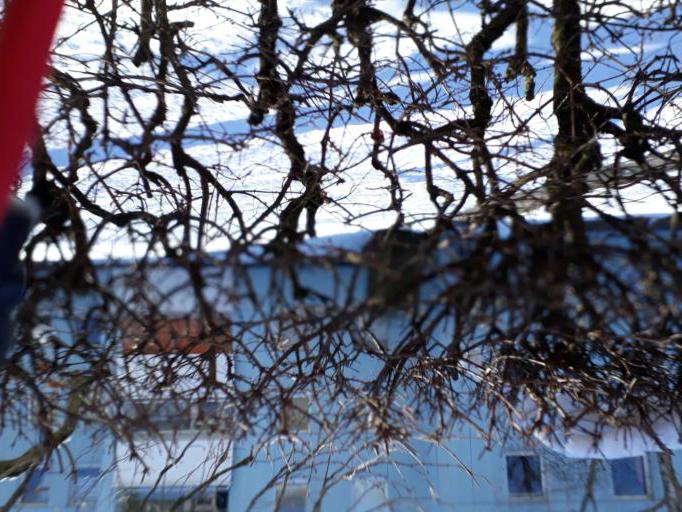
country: DE
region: Bavaria
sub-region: Upper Bavaria
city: Oberschleissheim
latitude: 48.2086
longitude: 11.5655
